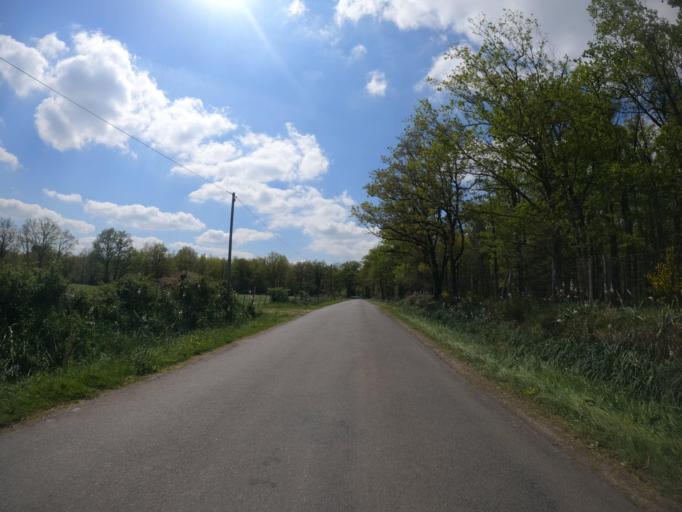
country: FR
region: Poitou-Charentes
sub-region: Departement des Deux-Sevres
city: Chiche
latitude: 46.7861
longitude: -0.3116
